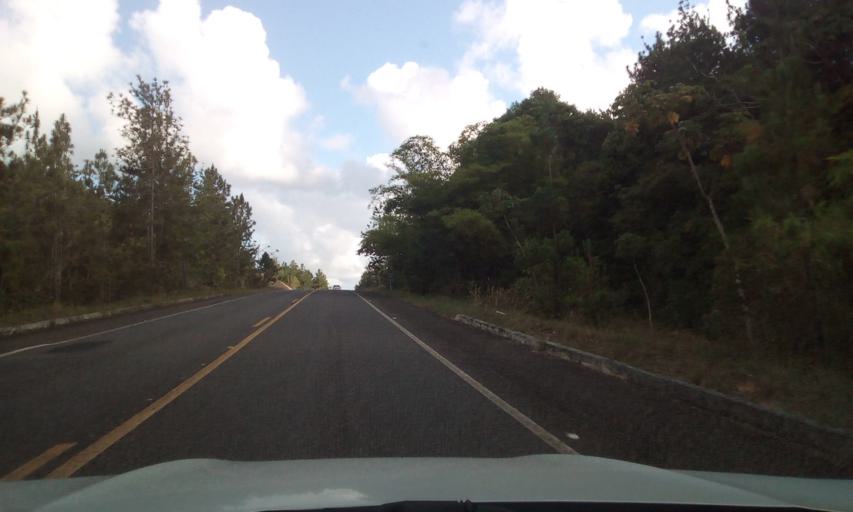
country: BR
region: Bahia
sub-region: Entre Rios
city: Entre Rios
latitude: -12.1157
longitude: -37.7870
